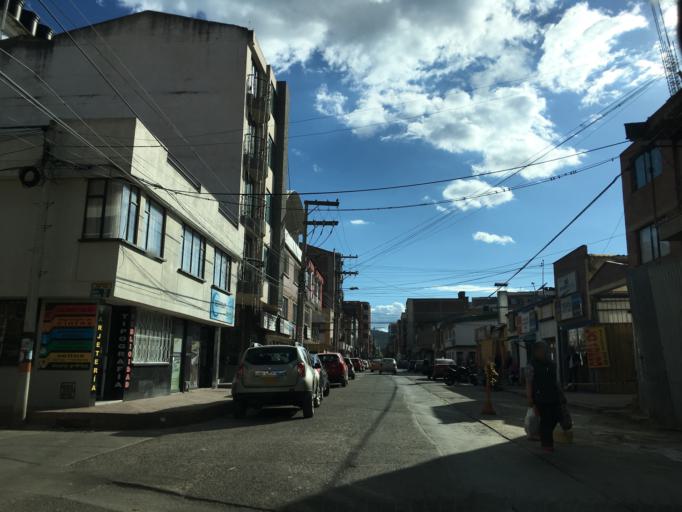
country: CO
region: Boyaca
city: Sogamoso
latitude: 5.7195
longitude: -72.9248
